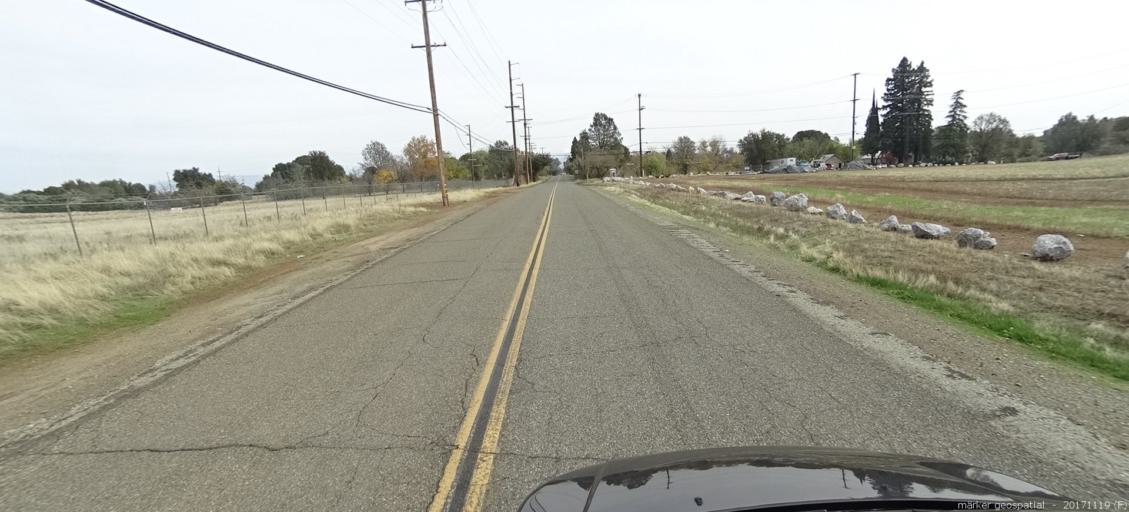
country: US
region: California
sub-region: Shasta County
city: Anderson
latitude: 40.4912
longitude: -122.2950
